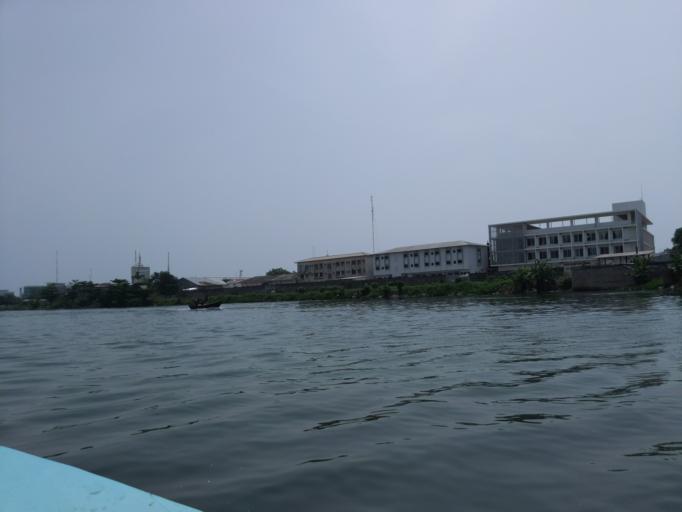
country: BJ
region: Littoral
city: Cotonou
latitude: 6.3633
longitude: 2.4391
